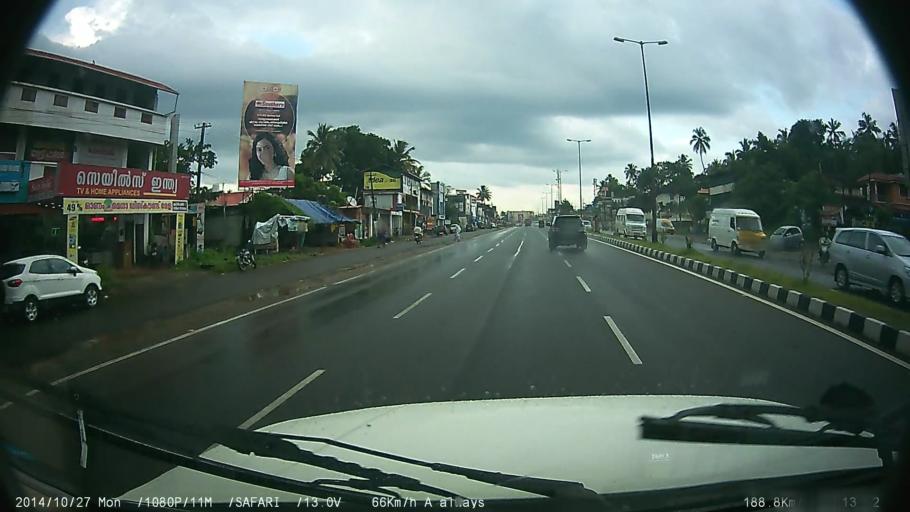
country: IN
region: Kerala
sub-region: Thrissur District
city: Irinjalakuda
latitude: 10.4185
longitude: 76.2702
